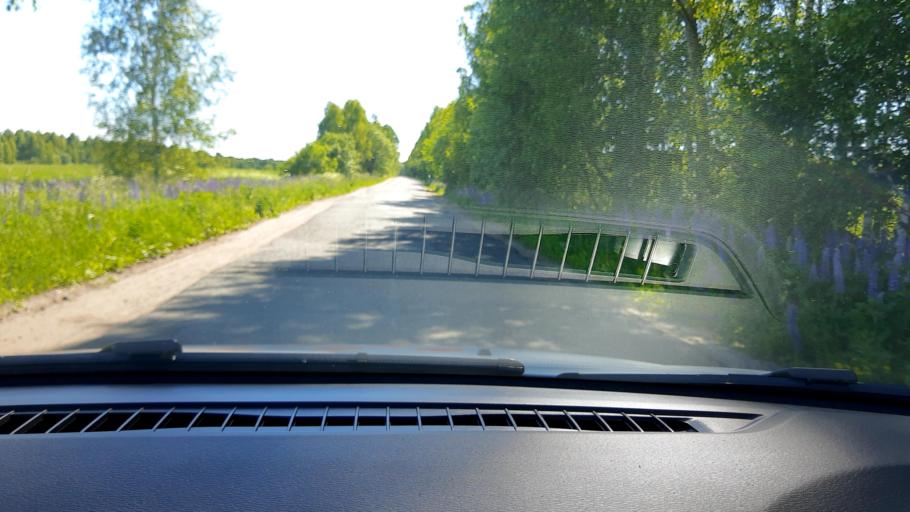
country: RU
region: Nizjnij Novgorod
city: Sitniki
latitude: 56.4422
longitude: 44.2032
